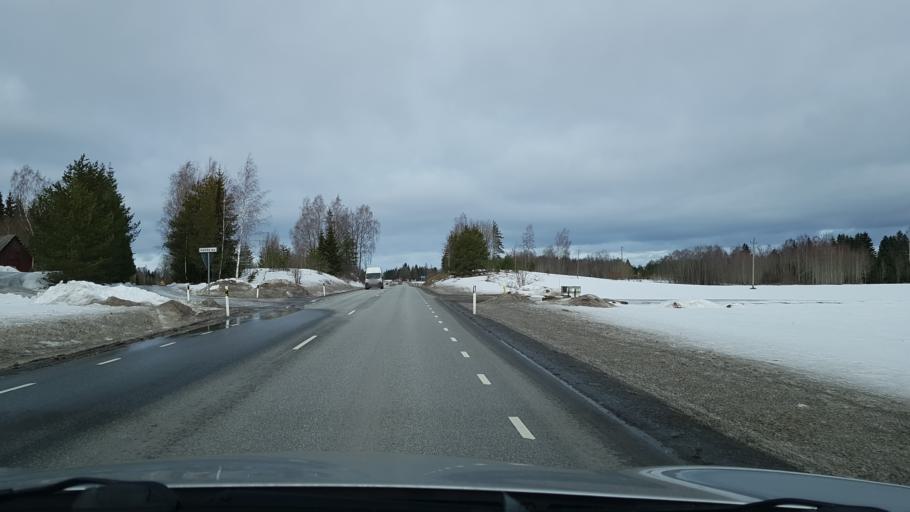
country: EE
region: Jogevamaa
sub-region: Jogeva linn
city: Jogeva
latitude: 58.7692
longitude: 26.3289
